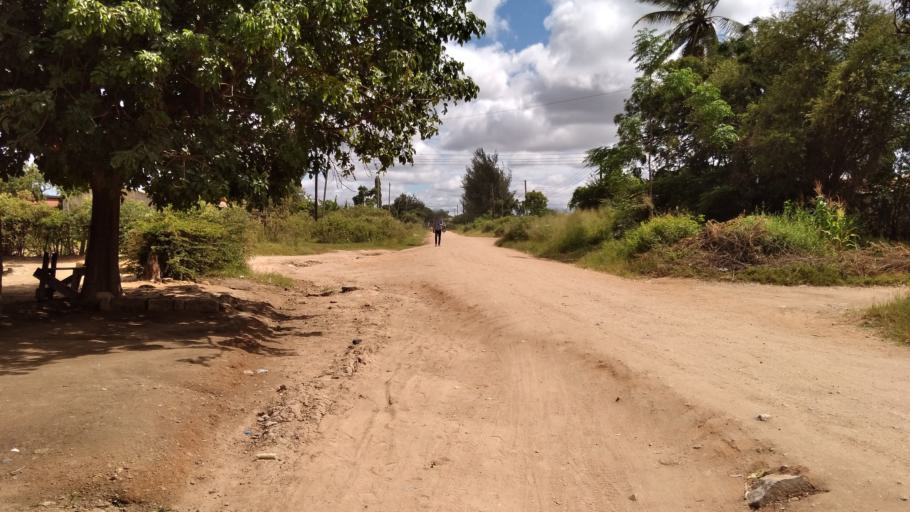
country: TZ
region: Dodoma
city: Dodoma
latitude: -6.1664
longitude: 35.7371
